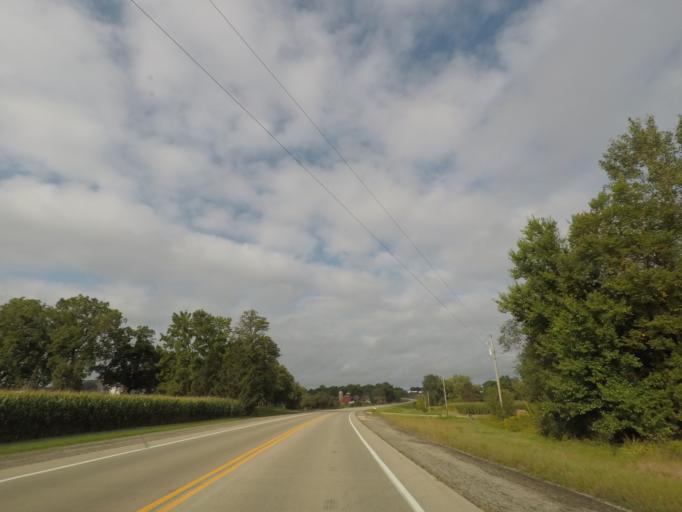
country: US
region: Wisconsin
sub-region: Dane County
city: Cottage Grove
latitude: 43.0286
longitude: -89.1677
